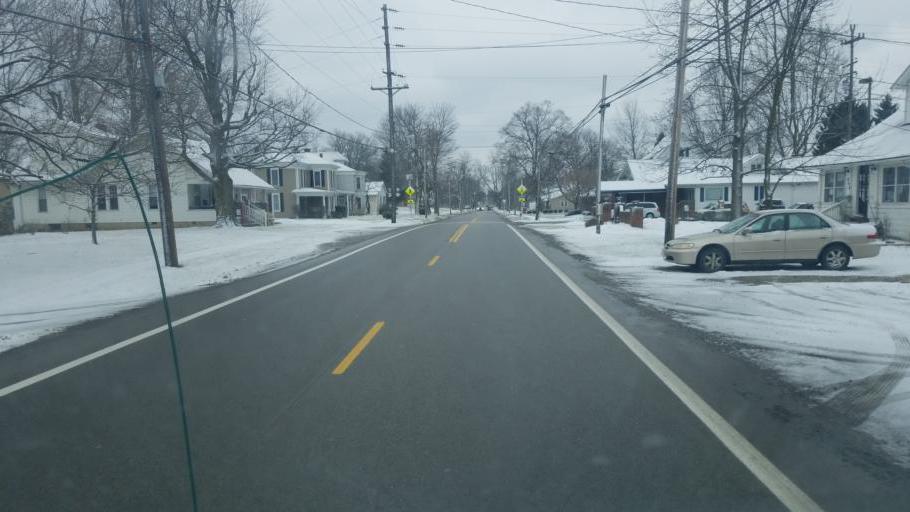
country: US
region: Ohio
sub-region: Licking County
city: Johnstown
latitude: 40.1581
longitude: -82.6890
